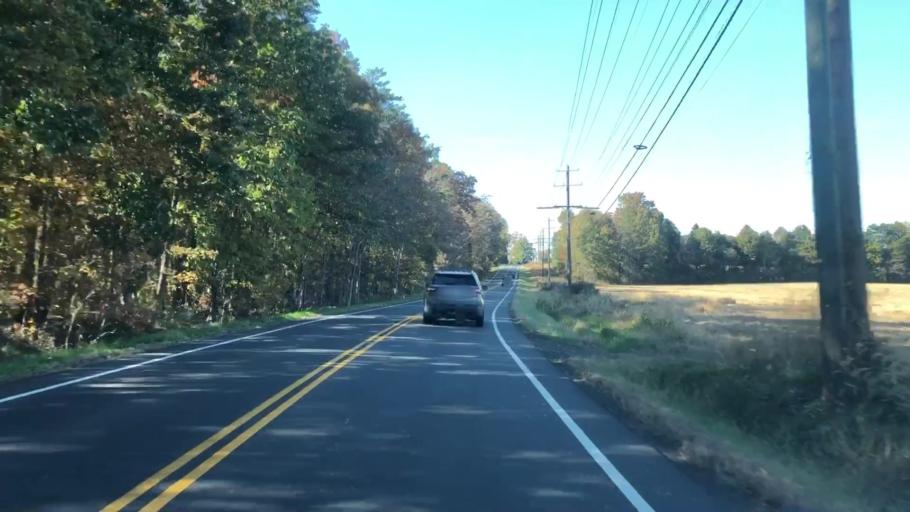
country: US
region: Virginia
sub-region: Prince William County
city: Linton Hall
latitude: 38.7379
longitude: -77.5995
